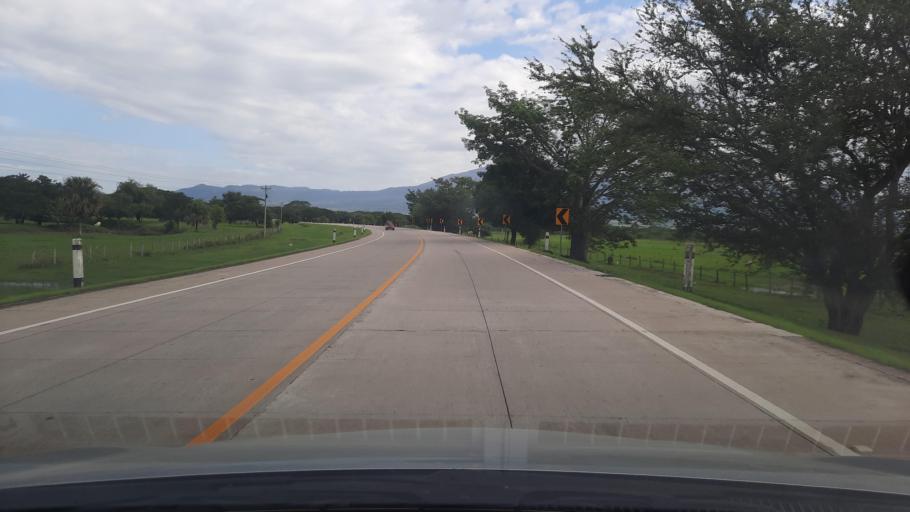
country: NI
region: Chinandega
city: Somotillo
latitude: 12.8139
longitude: -86.9021
